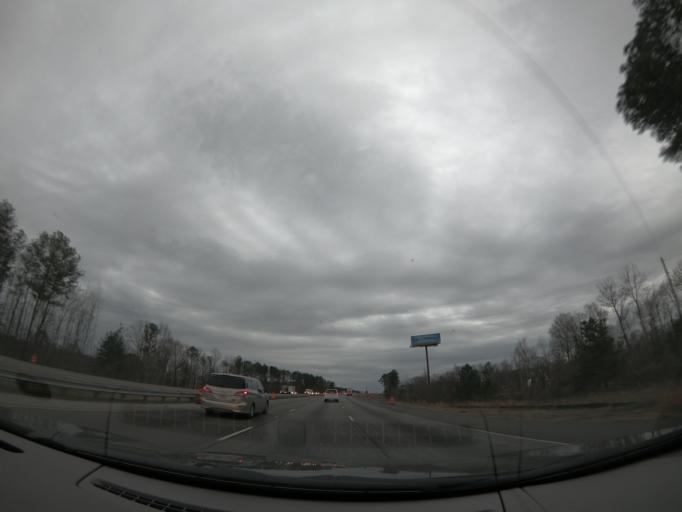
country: US
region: Georgia
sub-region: Whitfield County
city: Dalton
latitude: 34.6601
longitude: -84.9868
